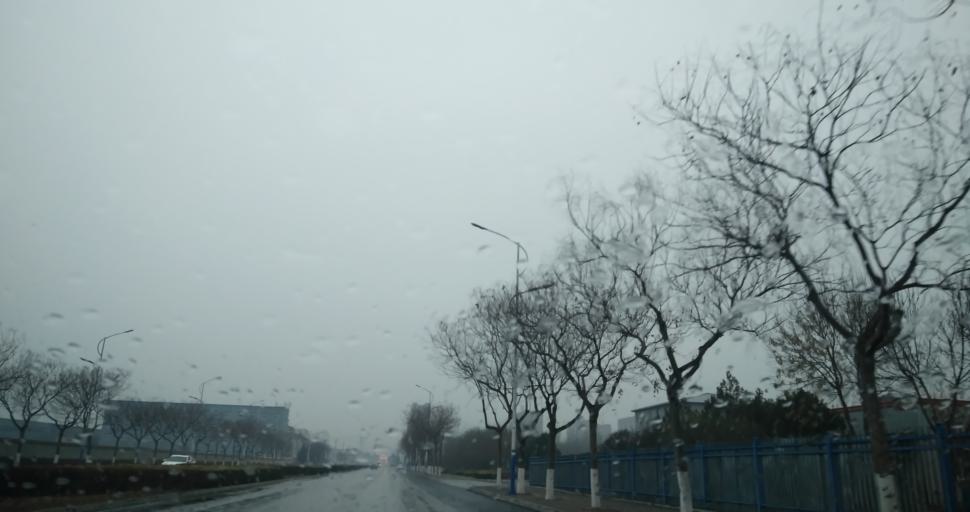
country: CN
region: Beijing
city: Yinghai
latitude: 39.7085
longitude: 116.4069
